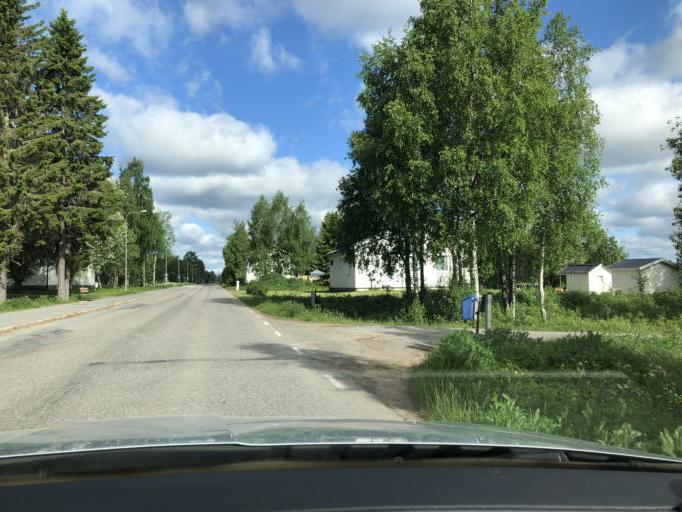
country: SE
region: Norrbotten
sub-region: Pajala Kommun
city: Pajala
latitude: 67.2193
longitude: 23.3529
